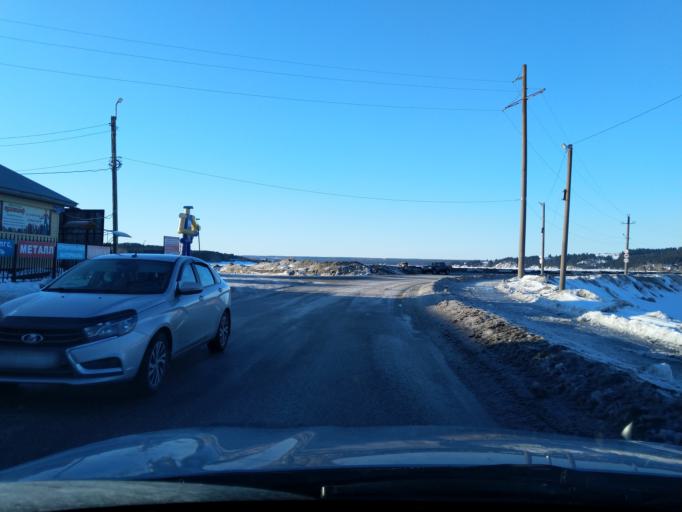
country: RU
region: Perm
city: Polazna
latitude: 58.3014
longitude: 56.4179
